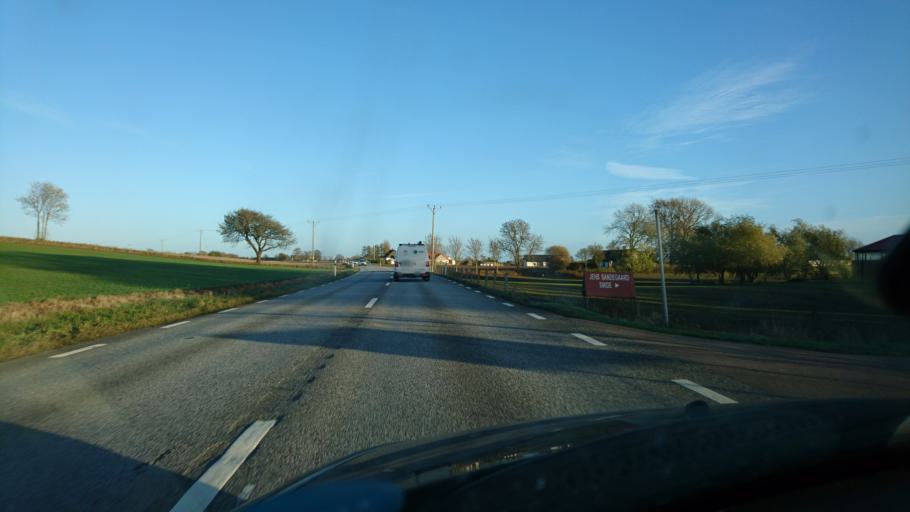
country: SE
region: Skane
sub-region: Tomelilla Kommun
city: Tomelilla
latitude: 55.5457
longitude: 14.0198
